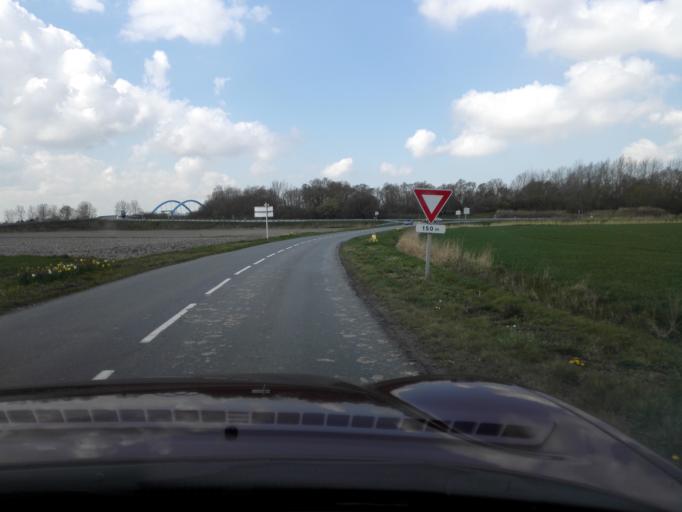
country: FR
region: Nord-Pas-de-Calais
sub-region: Departement du Nord
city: Brouckerque
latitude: 50.9554
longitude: 2.2754
